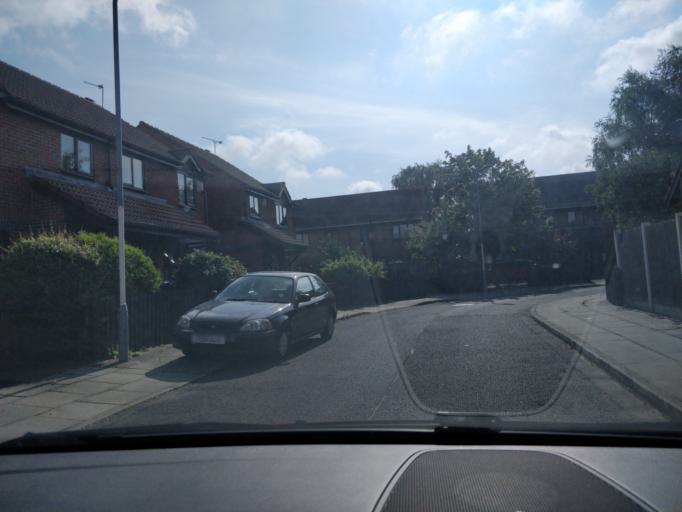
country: GB
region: England
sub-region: Sefton
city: Southport
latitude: 53.6481
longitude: -2.9610
